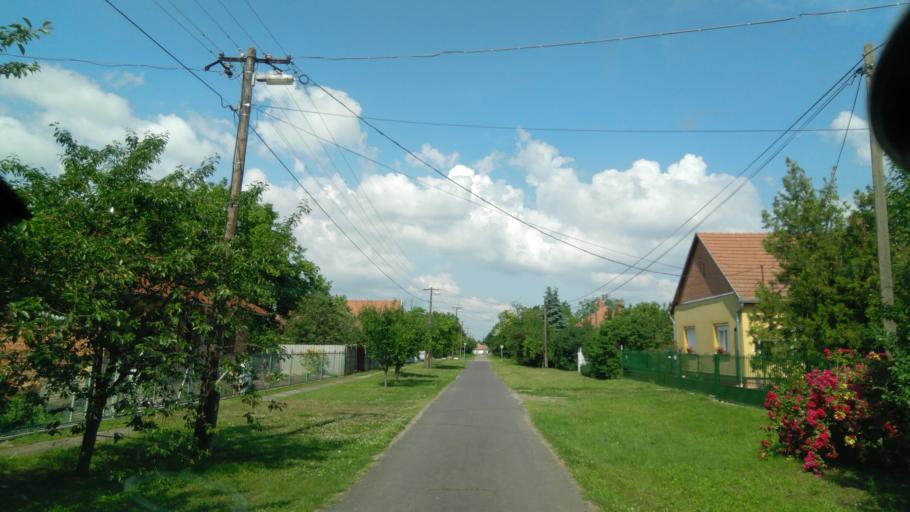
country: HU
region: Bekes
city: Doboz
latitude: 46.7381
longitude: 21.2302
